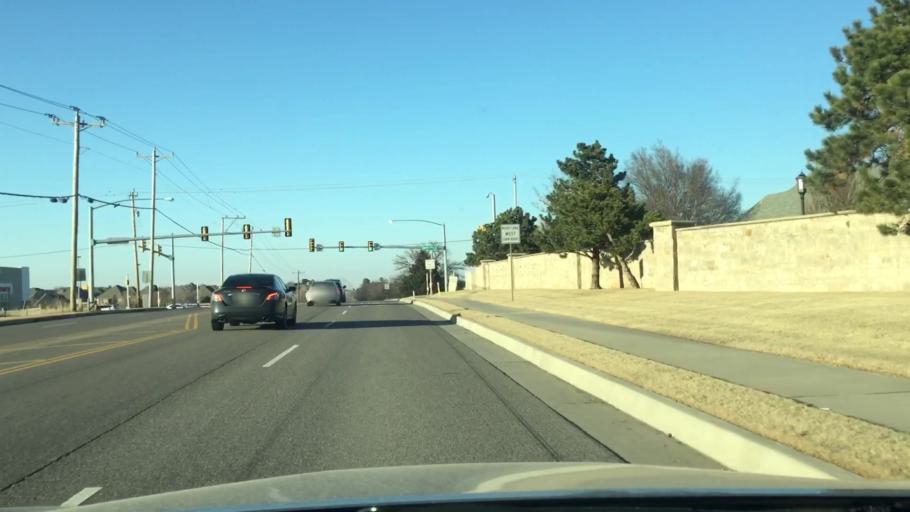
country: US
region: Oklahoma
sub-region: Oklahoma County
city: The Village
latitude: 35.6228
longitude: -97.6207
